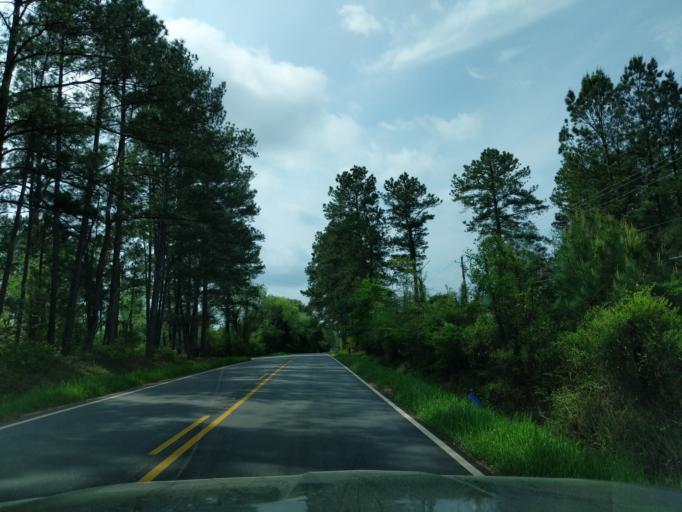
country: US
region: Georgia
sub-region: Columbia County
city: Appling
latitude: 33.6449
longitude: -82.3383
